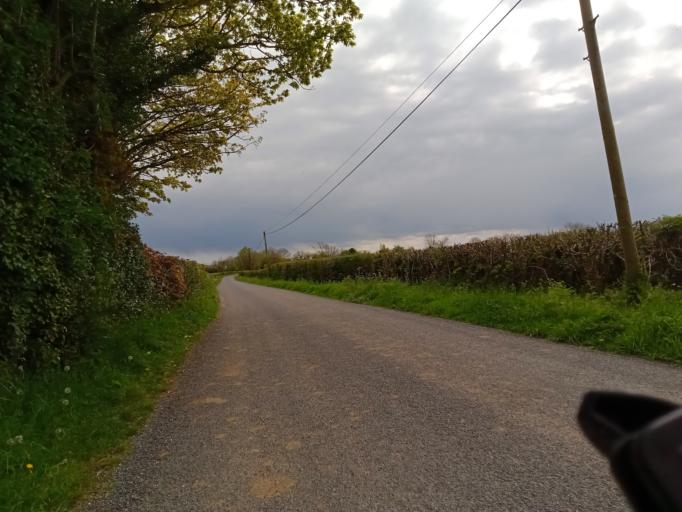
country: IE
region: Leinster
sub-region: Kilkenny
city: Kilkenny
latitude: 52.6194
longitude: -7.2968
